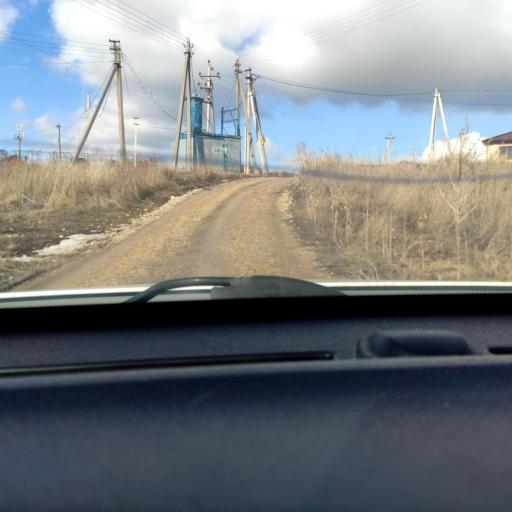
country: RU
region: Voronezj
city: Somovo
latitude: 51.6911
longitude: 39.3802
